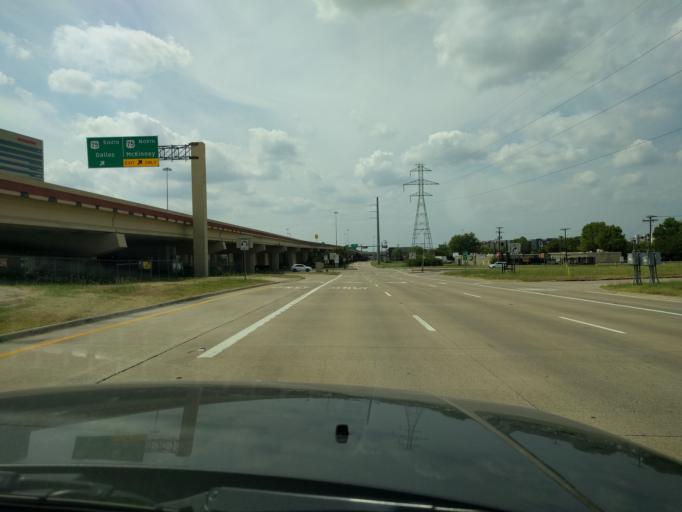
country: US
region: Texas
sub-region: Collin County
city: Plano
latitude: 33.0040
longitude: -96.6982
